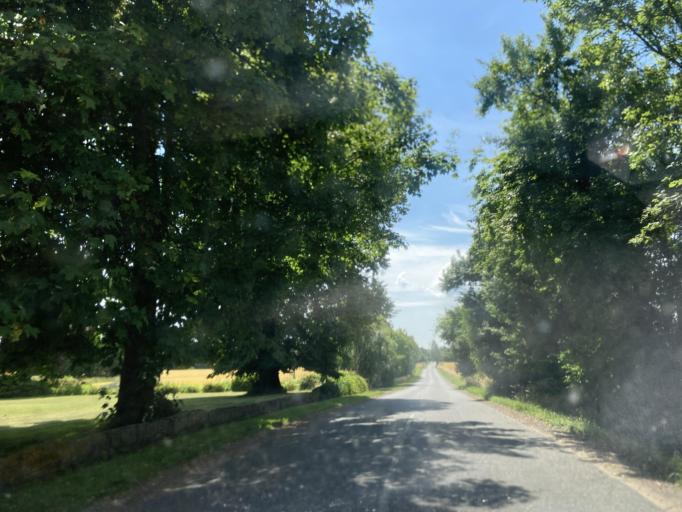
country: DK
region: Zealand
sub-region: Faxe Kommune
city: Haslev
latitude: 55.3974
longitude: 11.9412
